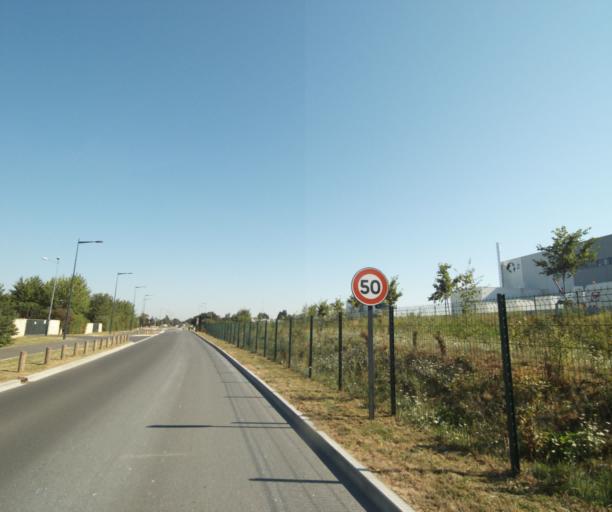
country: FR
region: Ile-de-France
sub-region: Departement de Seine-et-Marne
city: Moissy-Cramayel
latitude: 48.6167
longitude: 2.5815
